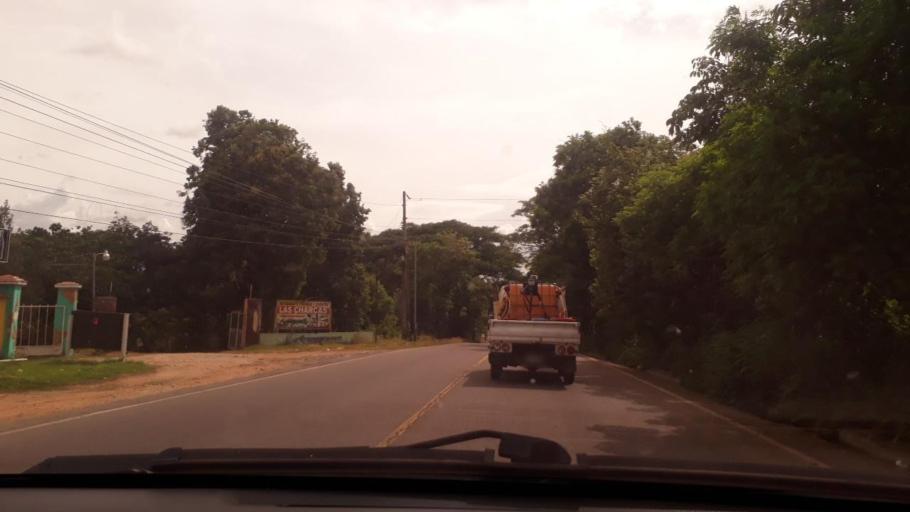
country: GT
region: Jutiapa
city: Jutiapa
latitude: 14.3007
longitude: -89.8825
